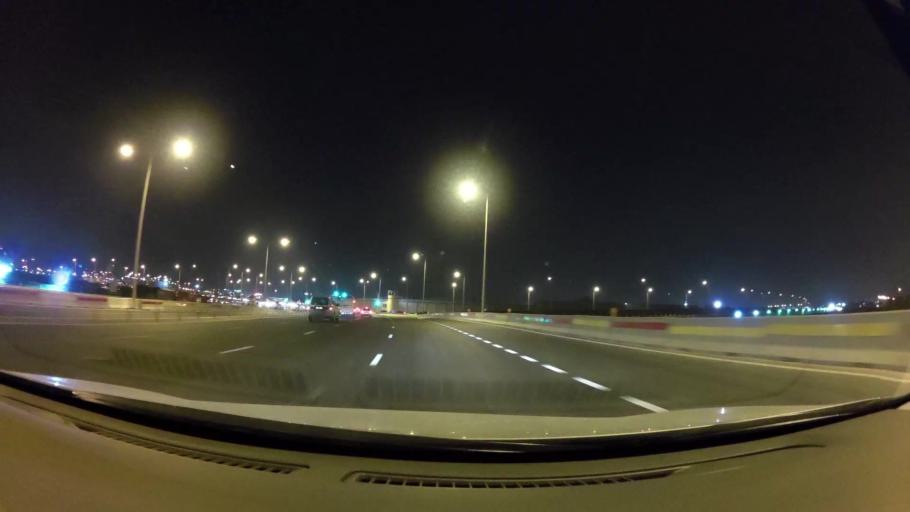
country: QA
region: Baladiyat ar Rayyan
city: Ar Rayyan
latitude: 25.2928
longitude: 51.4640
